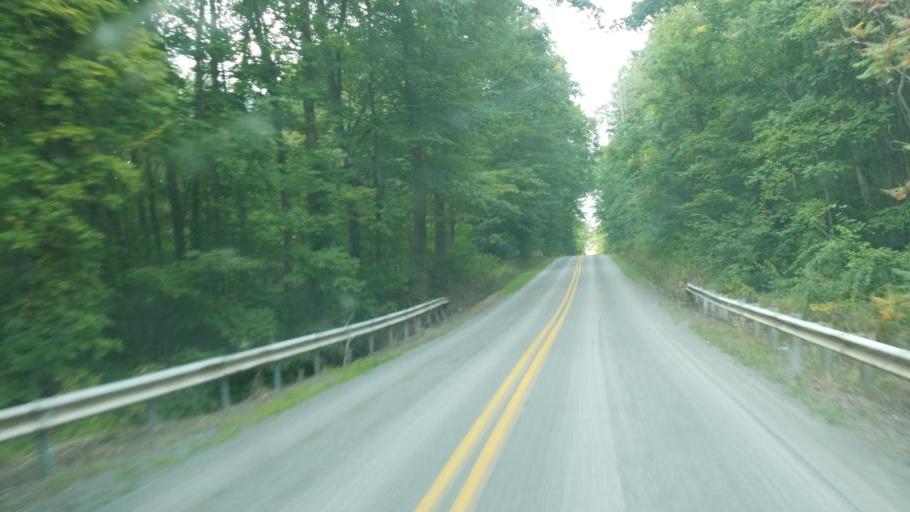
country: US
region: Pennsylvania
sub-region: Crawford County
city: Conneaut Lakeshore
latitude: 41.5183
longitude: -80.3373
